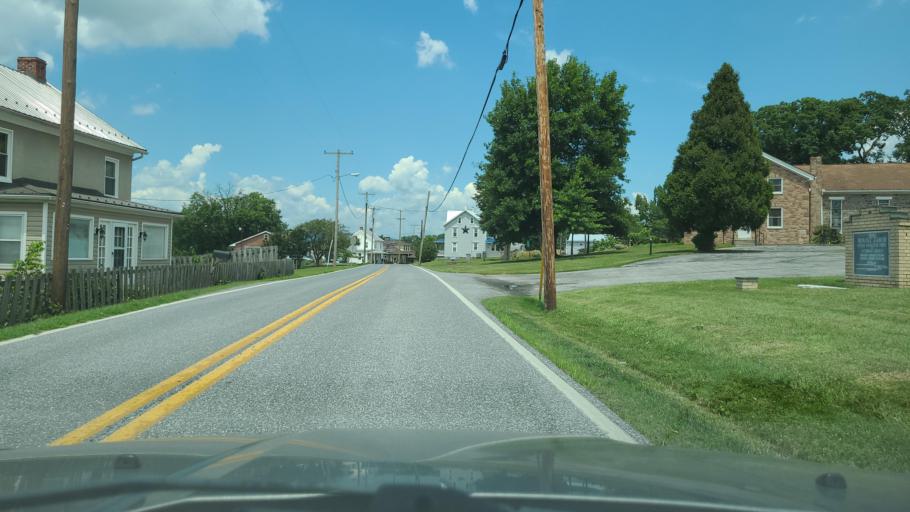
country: US
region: Maryland
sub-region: Frederick County
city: Woodsboro
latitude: 39.6038
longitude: -77.3182
